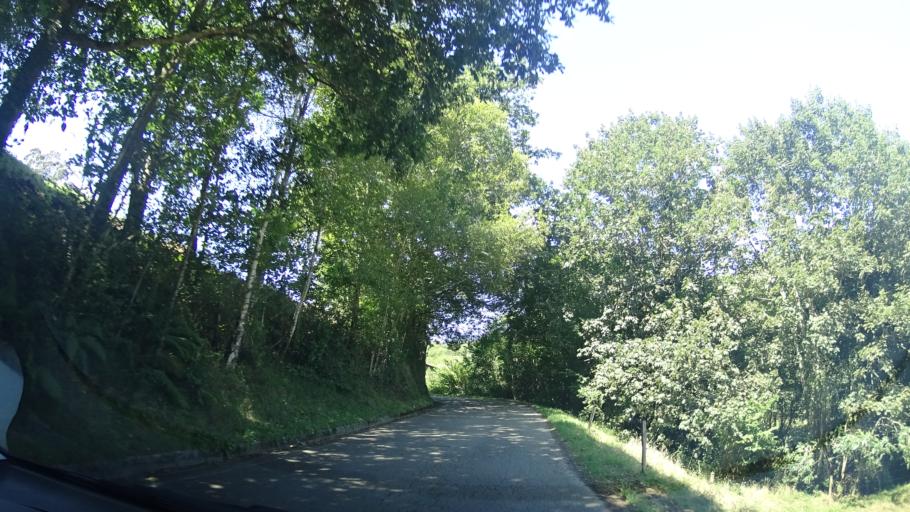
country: ES
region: Asturias
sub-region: Province of Asturias
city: Ribadesella
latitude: 43.4392
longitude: -5.0808
